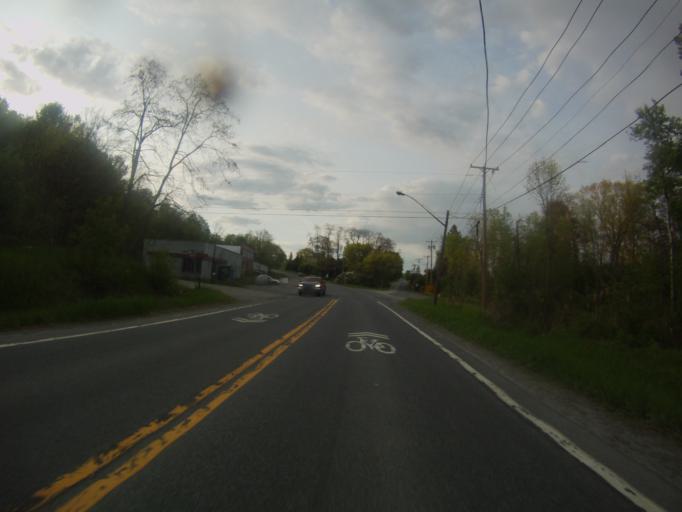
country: US
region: New York
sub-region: Essex County
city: Ticonderoga
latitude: 43.9473
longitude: -73.4176
